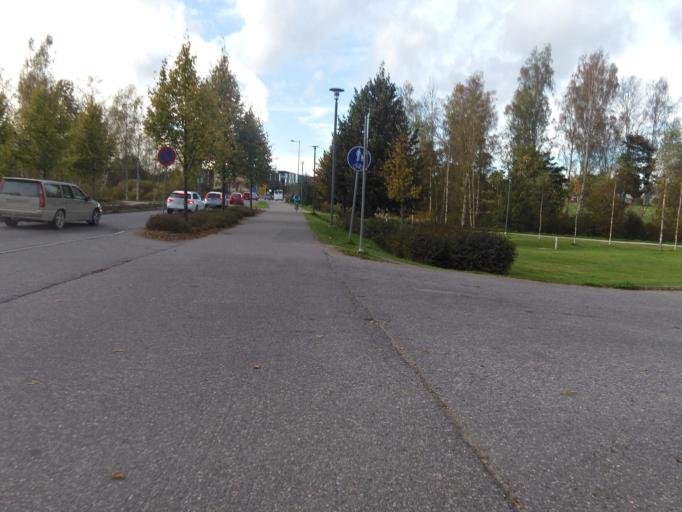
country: FI
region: Uusimaa
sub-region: Helsinki
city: Espoo
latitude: 60.2103
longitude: 24.6582
